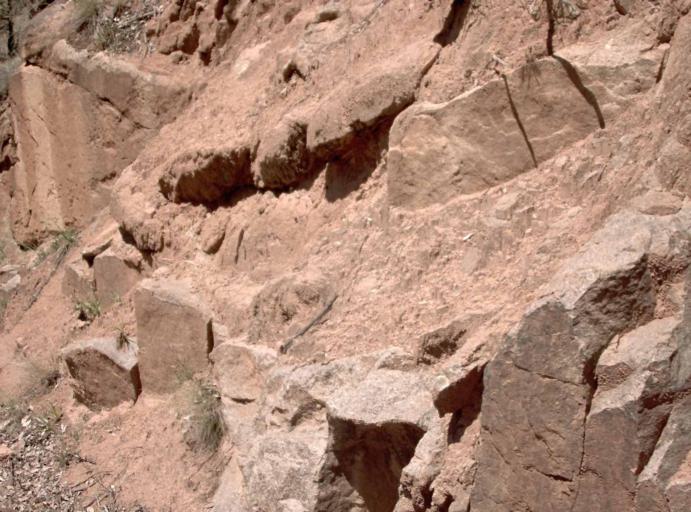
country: AU
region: New South Wales
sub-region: Snowy River
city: Jindabyne
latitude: -37.0662
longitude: 148.5043
